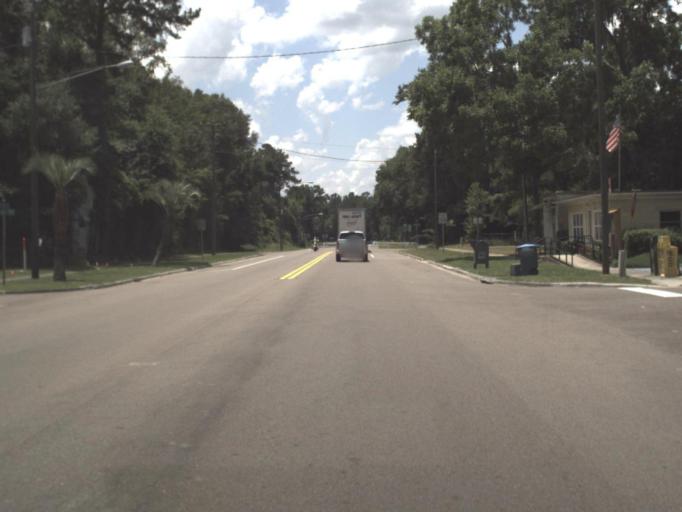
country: US
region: Florida
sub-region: Alachua County
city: Alachua
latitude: 29.8420
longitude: -82.4052
